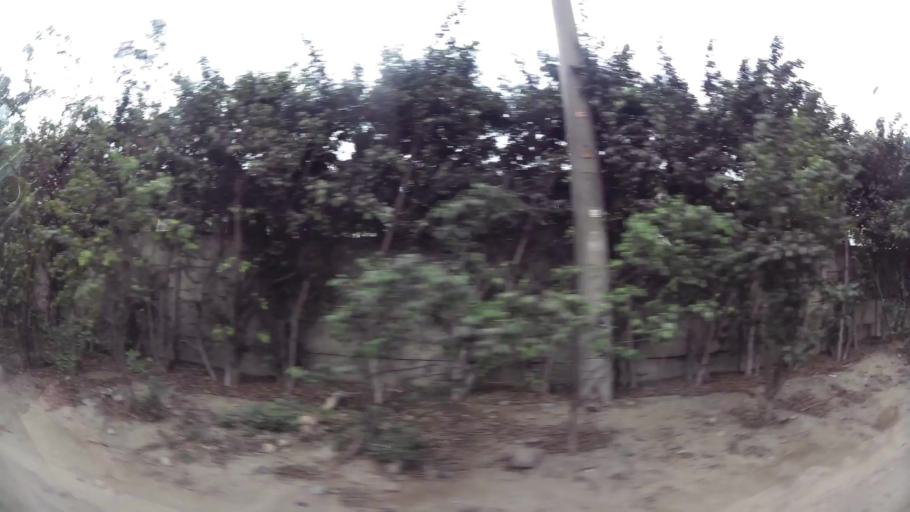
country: PE
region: Lima
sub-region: Lima
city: La Molina
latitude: -12.0857
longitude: -76.9164
